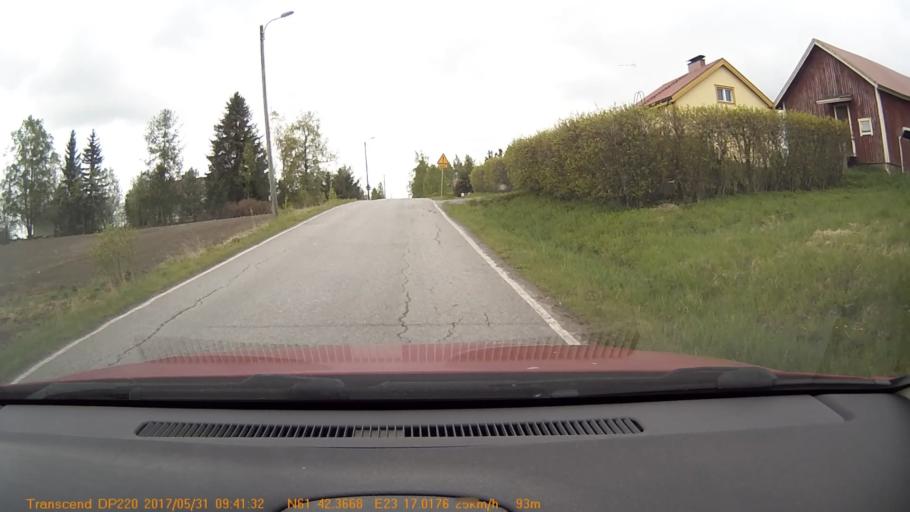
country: FI
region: Pirkanmaa
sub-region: Tampere
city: Viljakkala
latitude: 61.7060
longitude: 23.2834
